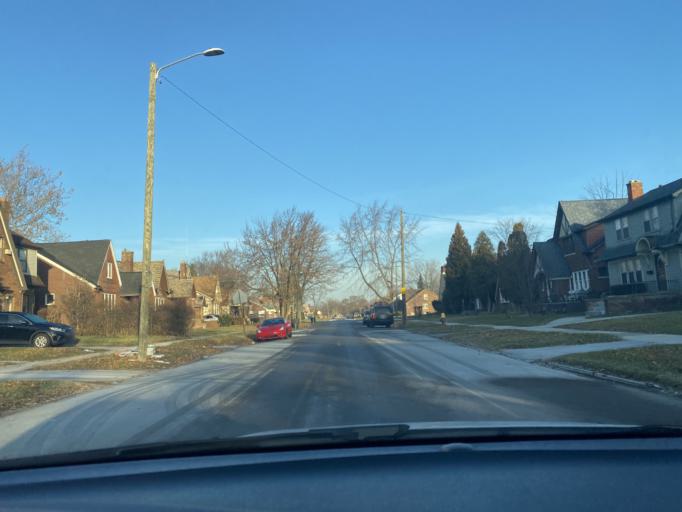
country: US
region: Michigan
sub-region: Wayne County
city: Grosse Pointe Park
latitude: 42.4039
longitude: -82.9493
